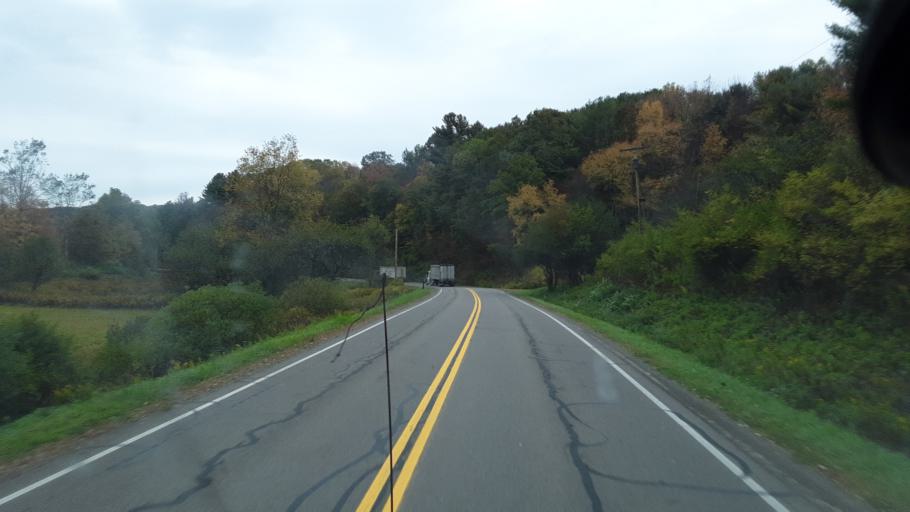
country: US
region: New York
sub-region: Allegany County
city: Andover
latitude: 42.0340
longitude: -77.7541
